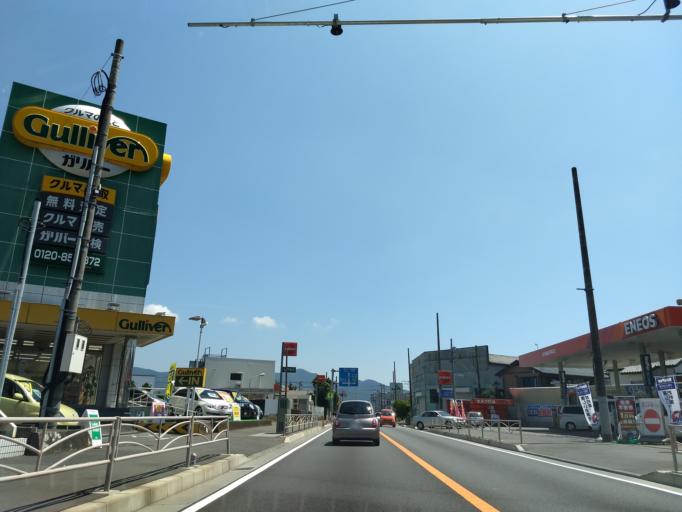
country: JP
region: Kanagawa
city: Hadano
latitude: 35.3727
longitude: 139.1991
